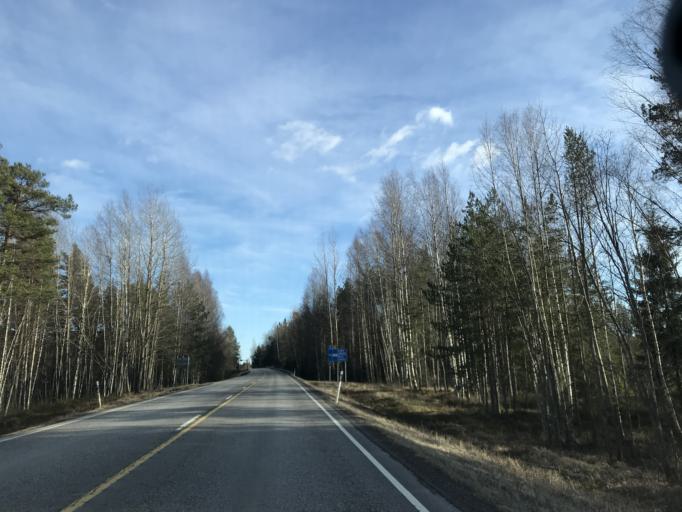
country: FI
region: Uusimaa
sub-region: Raaseporin
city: Ekenaes
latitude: 60.0699
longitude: 23.2725
